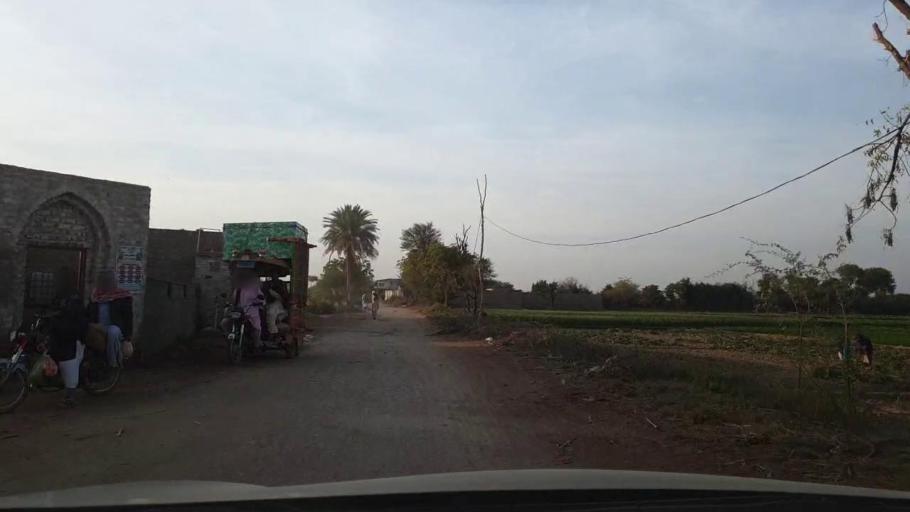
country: PK
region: Sindh
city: Tando Adam
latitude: 25.7115
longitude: 68.7237
